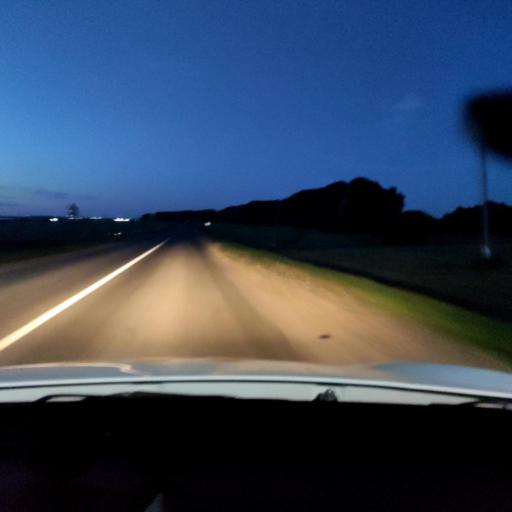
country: RU
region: Tatarstan
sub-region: Alekseyevskiy Rayon
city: Alekseyevskoye
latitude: 55.4151
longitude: 49.8617
